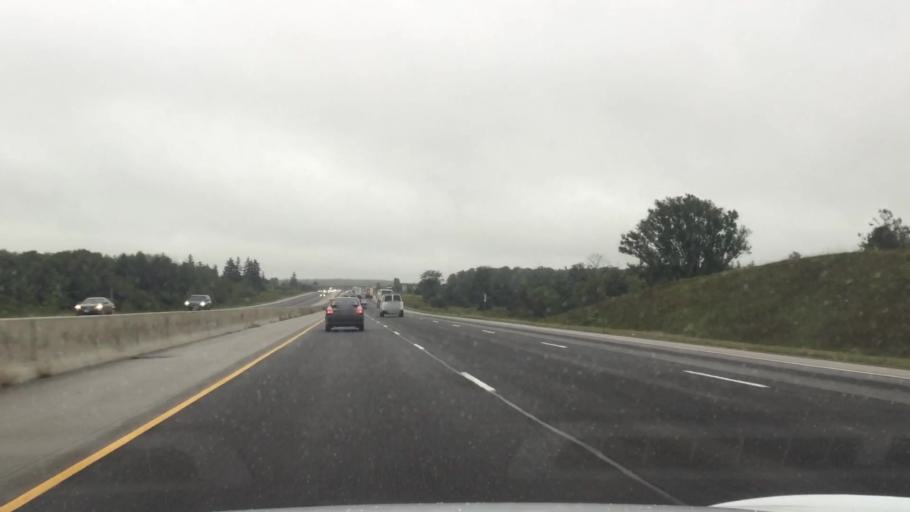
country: CA
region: Ontario
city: Kitchener
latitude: 43.3035
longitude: -80.4822
